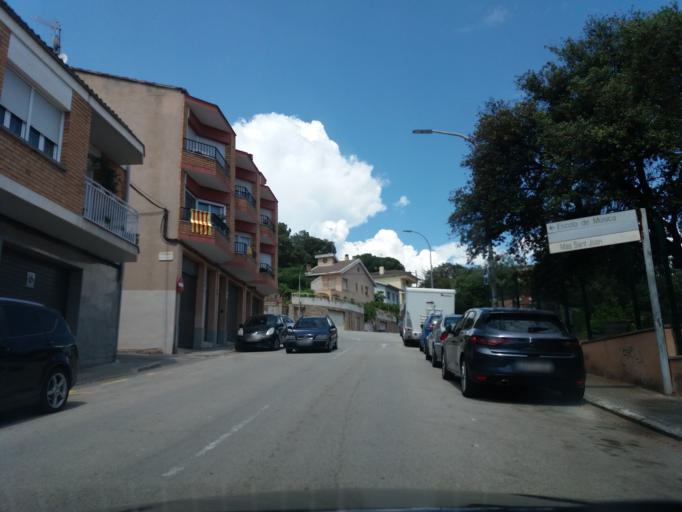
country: ES
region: Catalonia
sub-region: Provincia de Barcelona
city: Sant Joan de Vilatorrada
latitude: 41.7428
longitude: 1.8034
